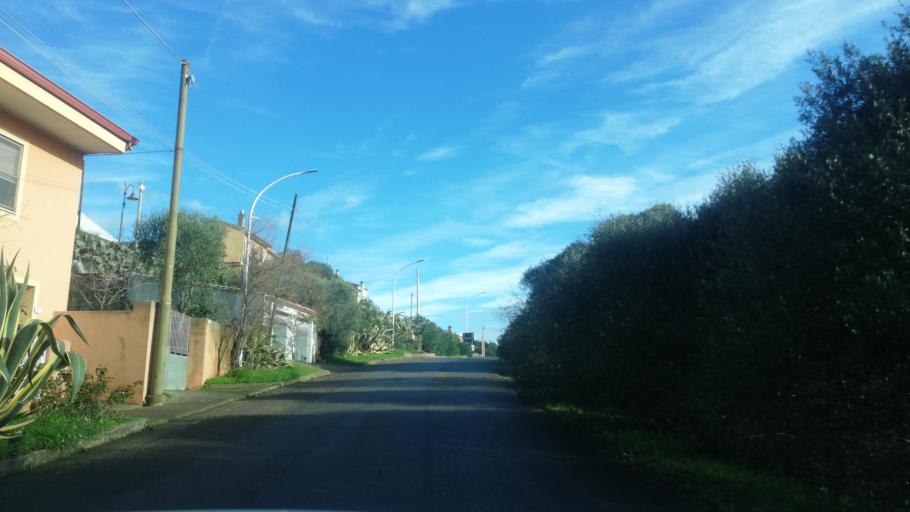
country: IT
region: Sardinia
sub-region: Provincia di Medio Campidano
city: Villanovaforru
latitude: 39.6304
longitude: 8.8723
